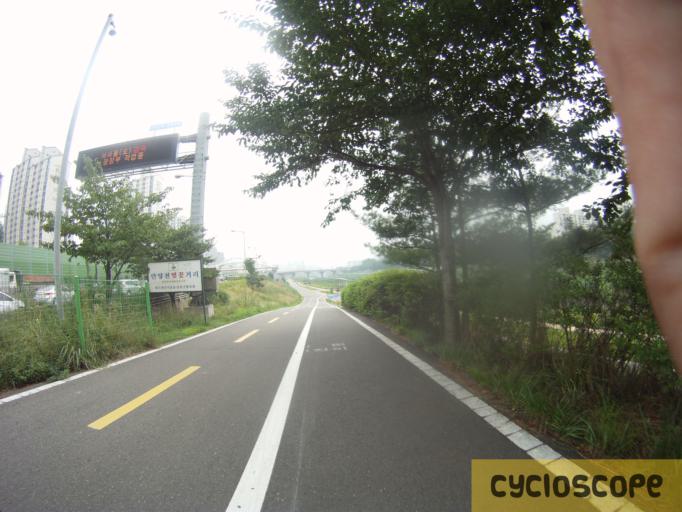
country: KR
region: Gyeonggi-do
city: Kwangmyong
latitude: 37.4617
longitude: 126.8891
